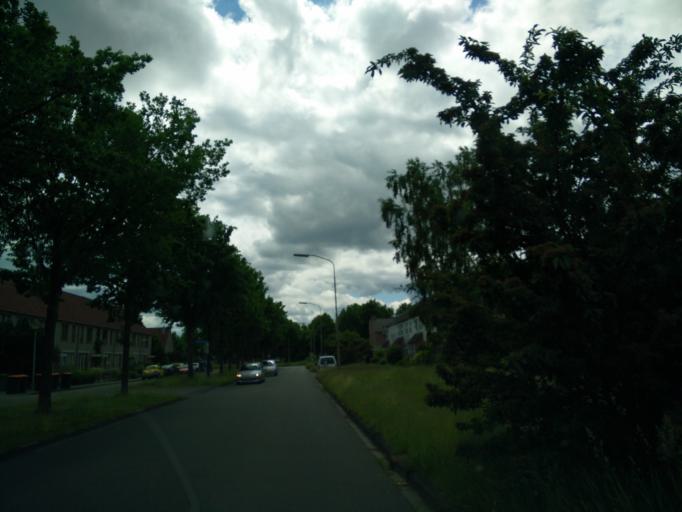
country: NL
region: Drenthe
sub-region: Gemeente Assen
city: Assen
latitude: 53.0206
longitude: 6.5824
